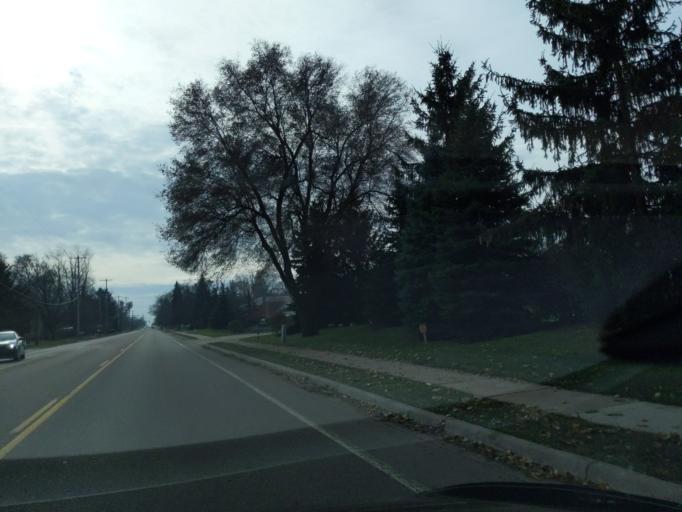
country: US
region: Michigan
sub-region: Ingham County
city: Holt
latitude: 42.6527
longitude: -84.5235
